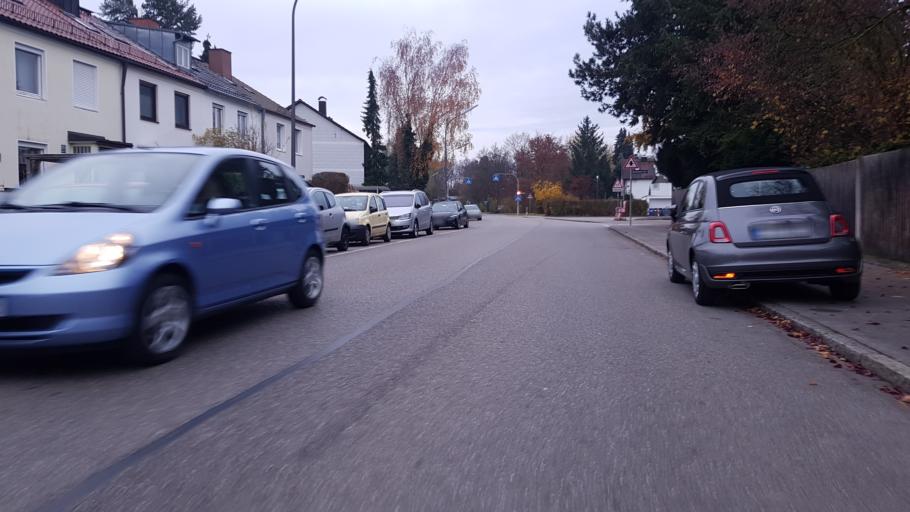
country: DE
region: Bavaria
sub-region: Upper Bavaria
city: Neubiberg
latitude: 48.1086
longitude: 11.6272
